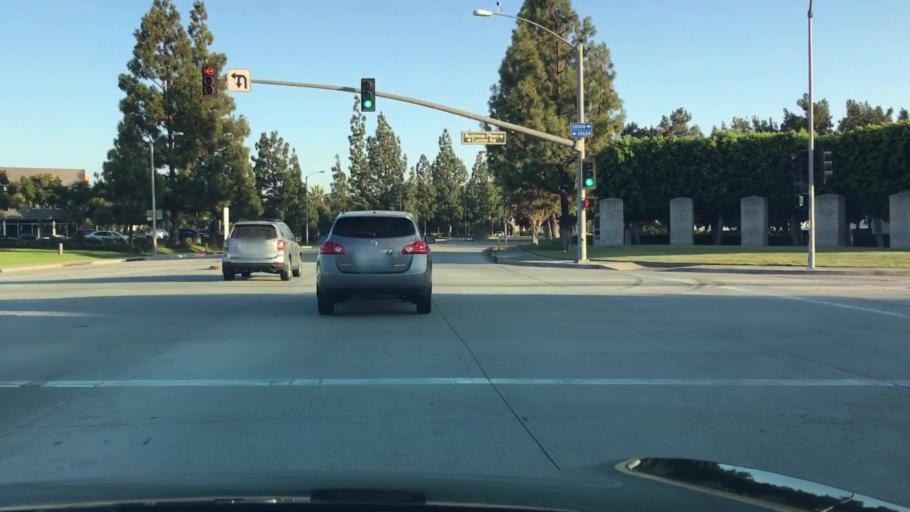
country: US
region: California
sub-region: Los Angeles County
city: Walnut
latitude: 34.0060
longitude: -117.8557
